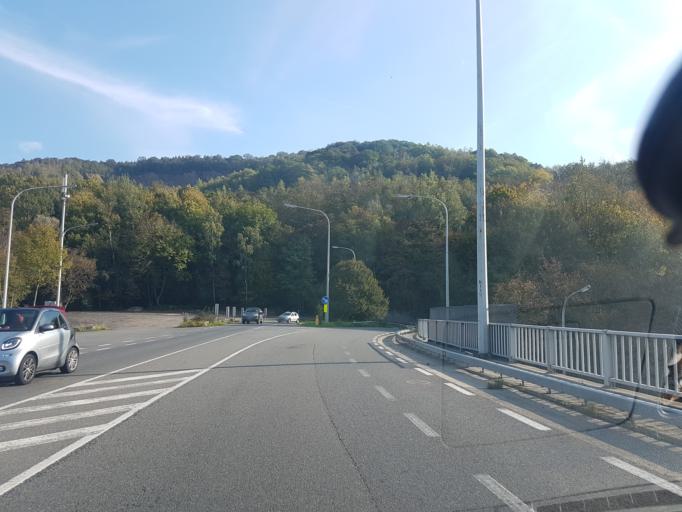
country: BE
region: Wallonia
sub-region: Province de Namur
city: Profondeville
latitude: 50.3981
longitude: 4.8828
